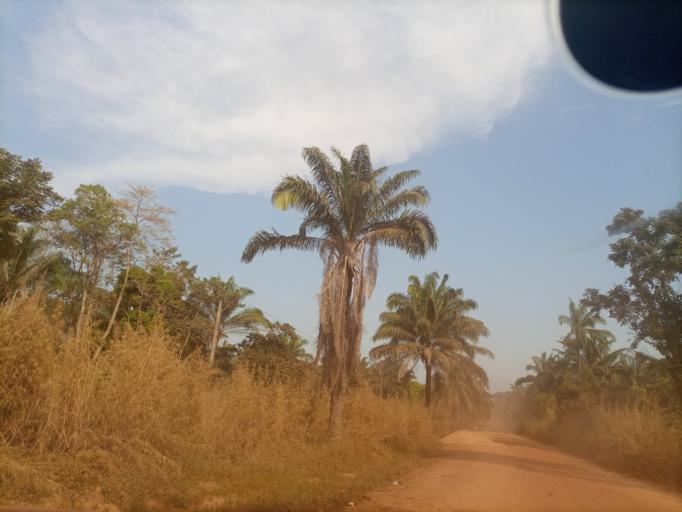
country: NG
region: Enugu
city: Obolo-Eke (1)
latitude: 6.8086
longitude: 7.5554
